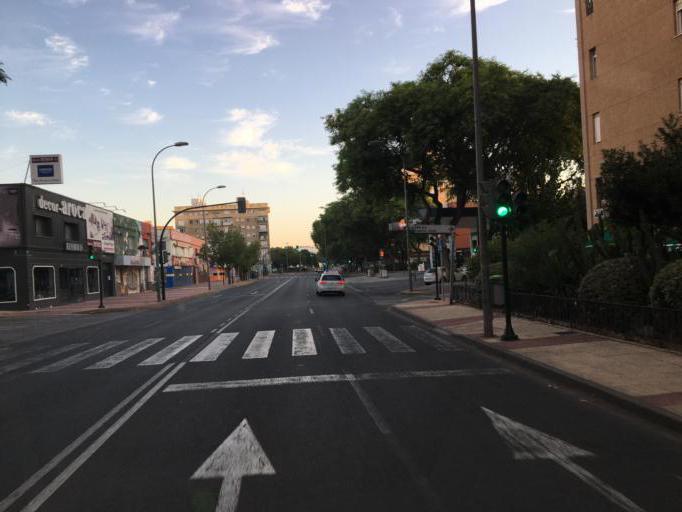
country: ES
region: Murcia
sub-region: Murcia
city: Murcia
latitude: 37.9959
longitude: -1.1426
